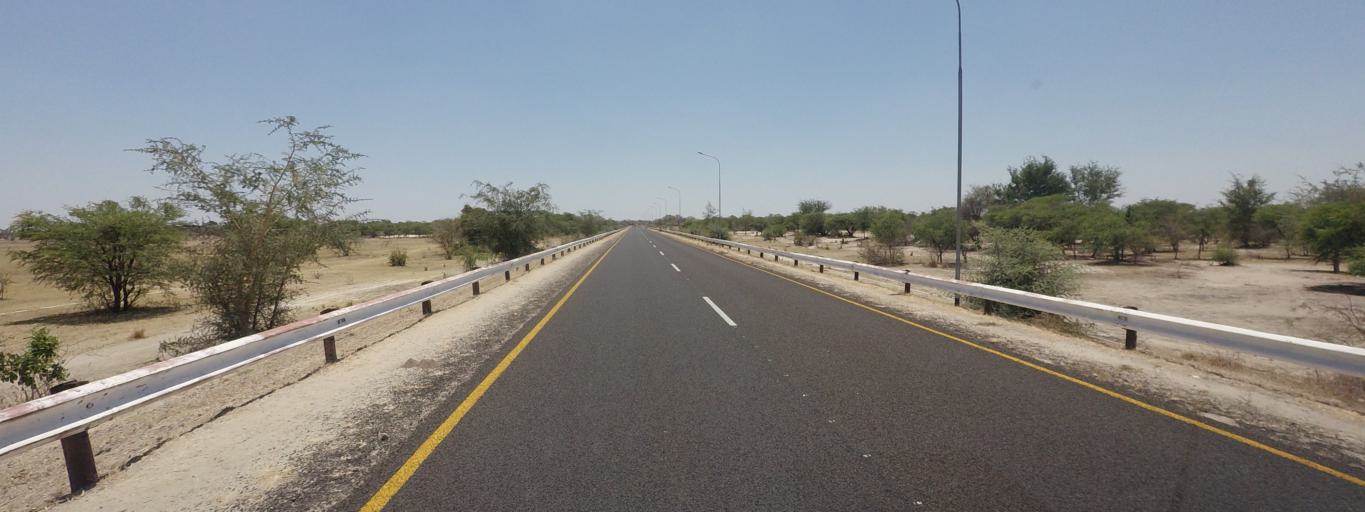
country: ZM
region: Western
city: Sesheke
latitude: -17.7232
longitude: 24.5219
